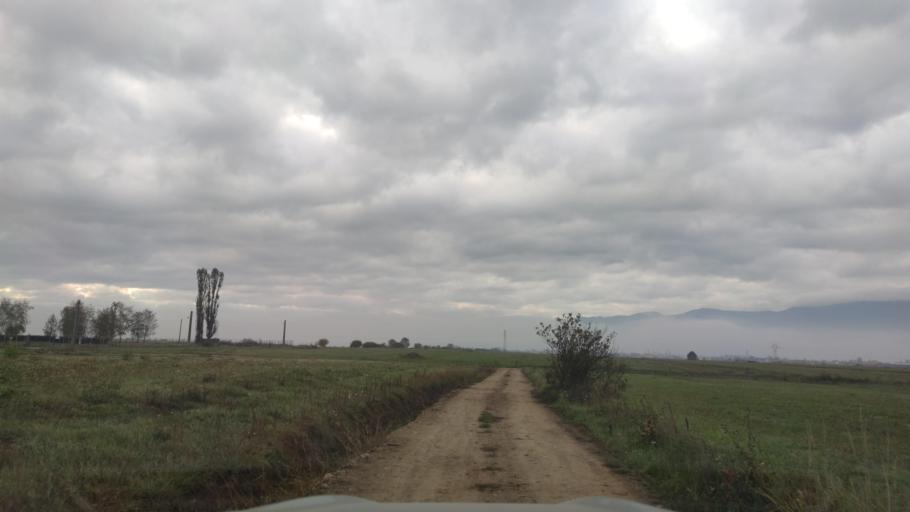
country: RO
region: Harghita
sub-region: Comuna Ciumani
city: Ciumani
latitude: 46.6977
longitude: 25.5197
